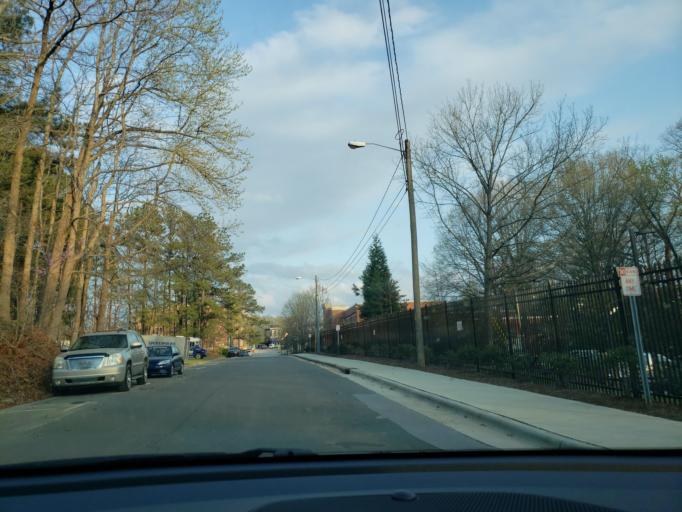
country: US
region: North Carolina
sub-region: Wake County
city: Apex
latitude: 35.7326
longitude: -78.8533
